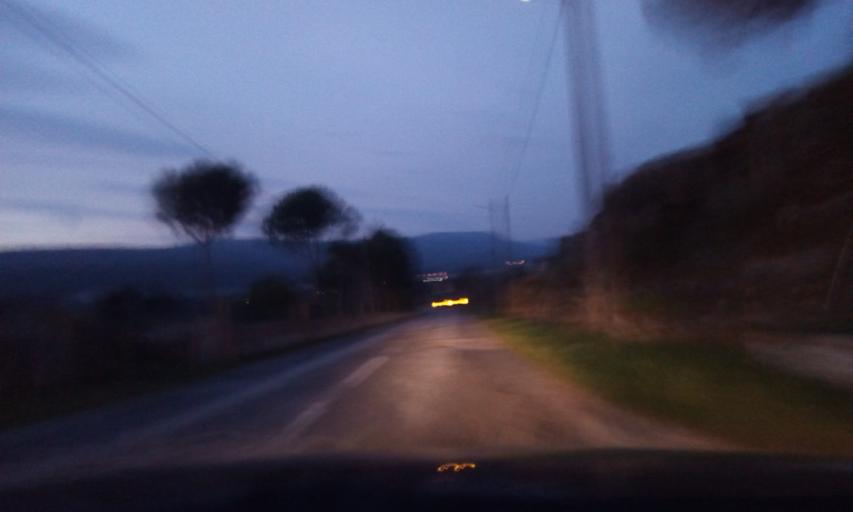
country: PT
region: Guarda
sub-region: Celorico da Beira
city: Celorico da Beira
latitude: 40.6269
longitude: -7.4330
